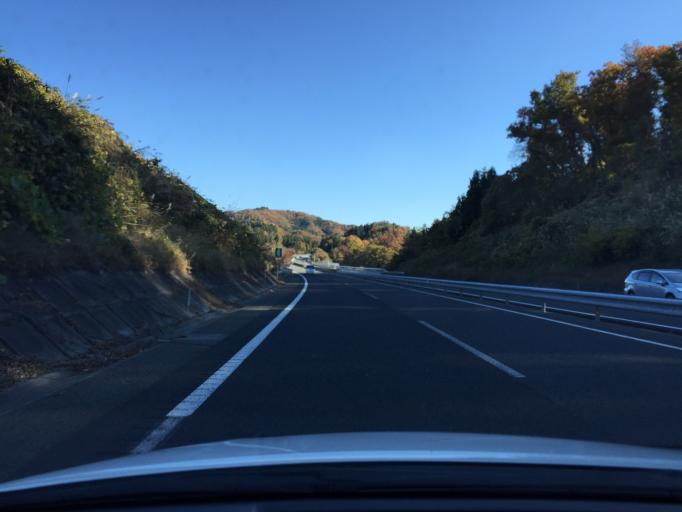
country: JP
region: Fukushima
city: Funehikimachi-funehiki
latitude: 37.4258
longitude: 140.5524
